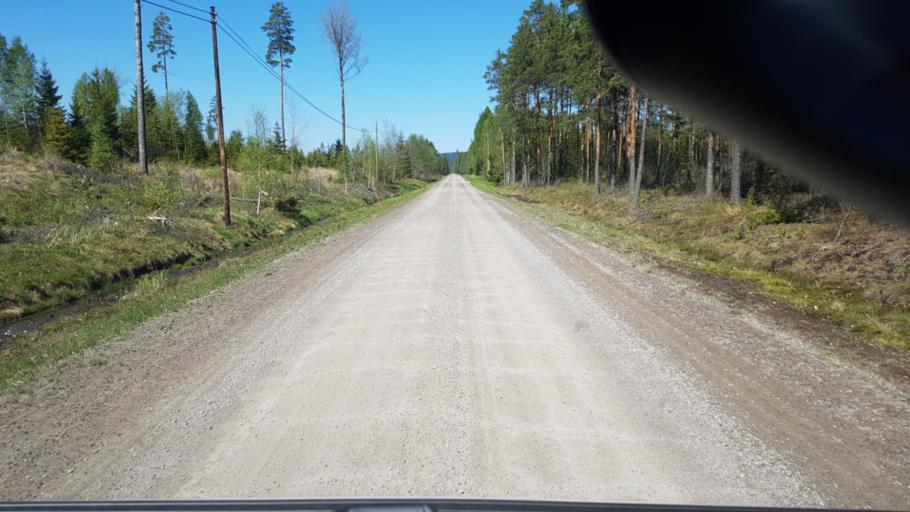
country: SE
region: Vaermland
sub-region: Eda Kommun
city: Charlottenberg
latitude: 59.9510
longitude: 12.5163
